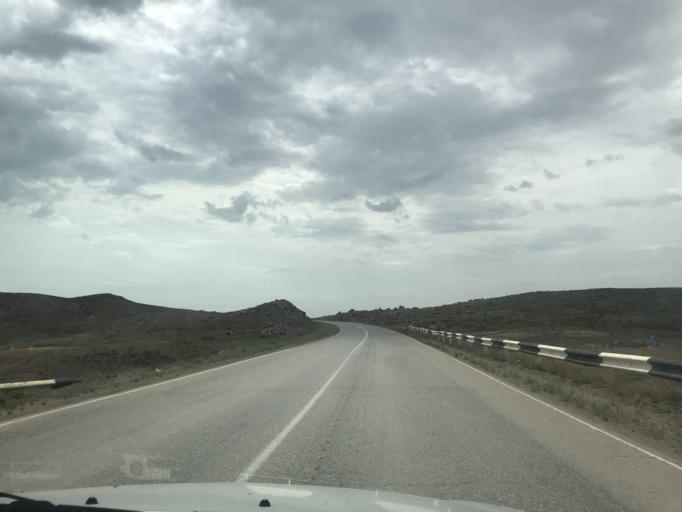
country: KZ
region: Zhambyl
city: Mynaral
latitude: 45.5106
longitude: 73.4981
